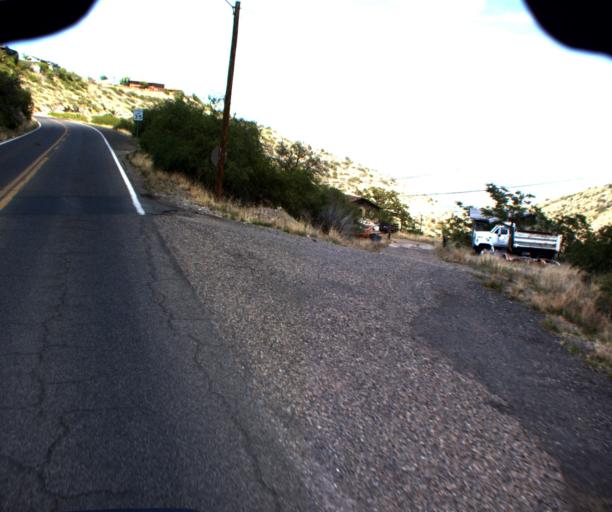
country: US
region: Arizona
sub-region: Yavapai County
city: Clarkdale
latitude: 34.7459
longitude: -112.1099
